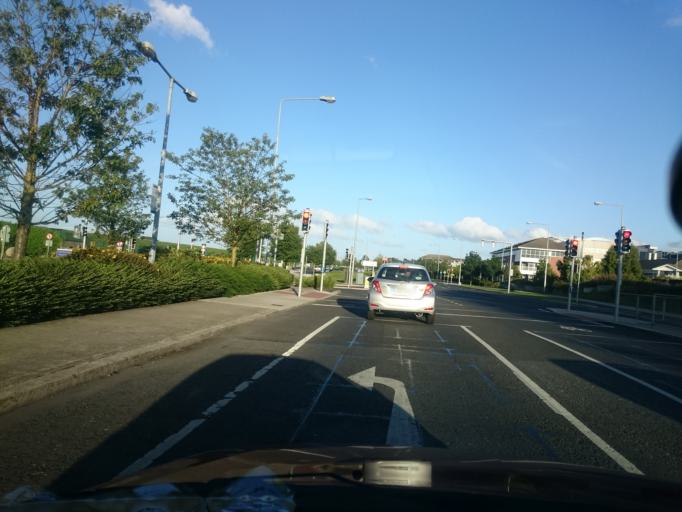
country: IE
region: Leinster
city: Sandyford
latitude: 53.2795
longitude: -6.2115
